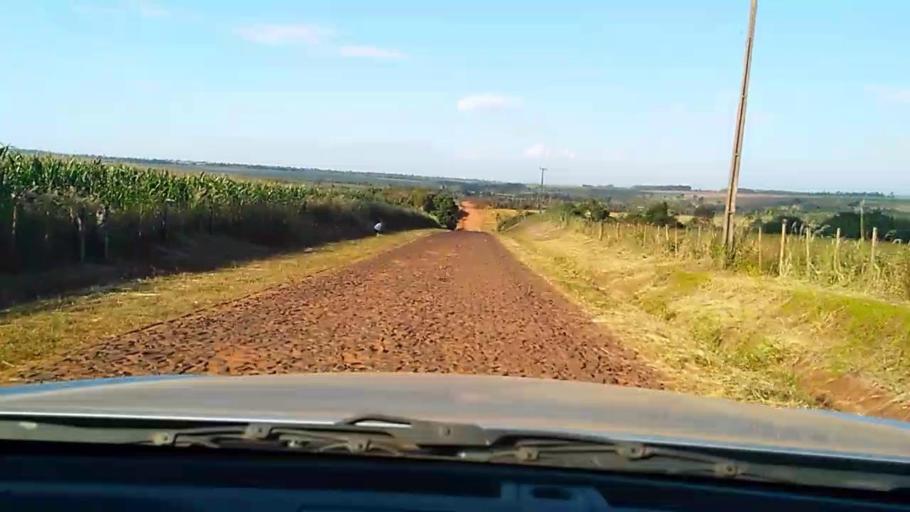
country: PY
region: Alto Parana
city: Doctor Juan Leon Mallorquin
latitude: -25.6972
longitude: -55.3806
